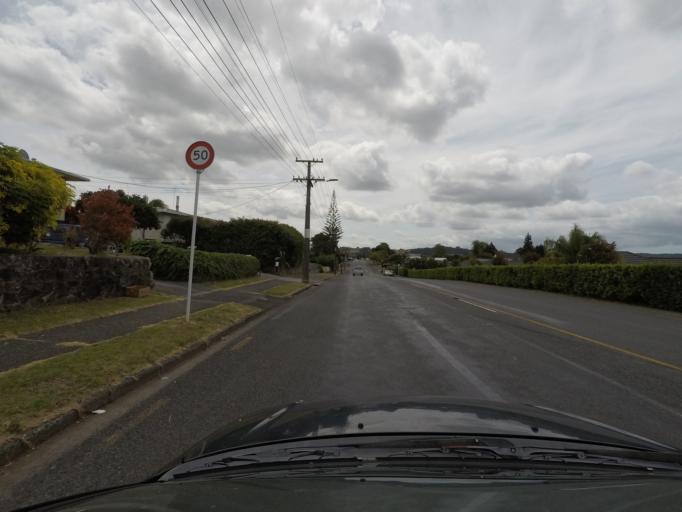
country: NZ
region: Northland
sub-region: Whangarei
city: Whangarei
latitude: -35.6828
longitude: 174.3265
